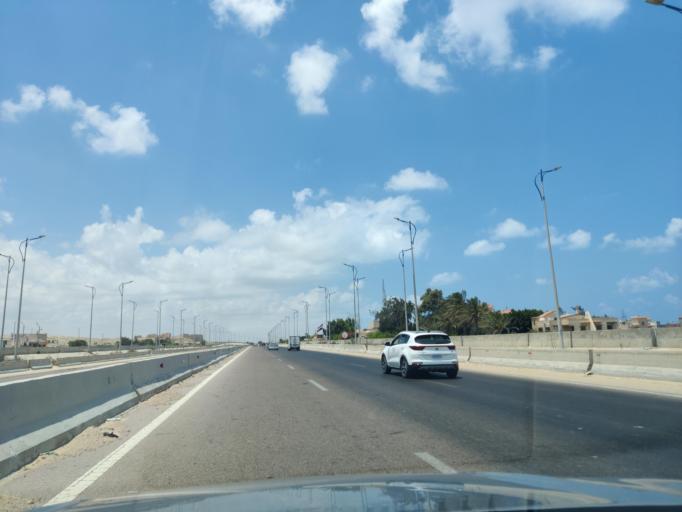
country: EG
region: Alexandria
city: Alexandria
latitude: 30.9523
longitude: 29.5269
